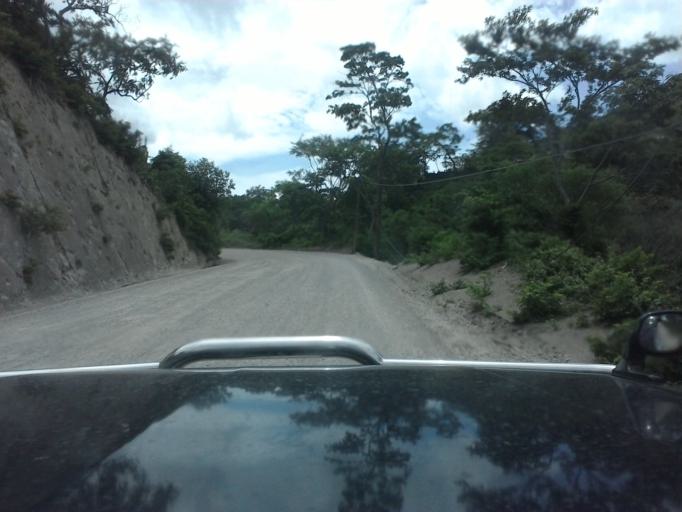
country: CR
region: Guanacaste
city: Juntas
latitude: 10.2389
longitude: -84.8524
